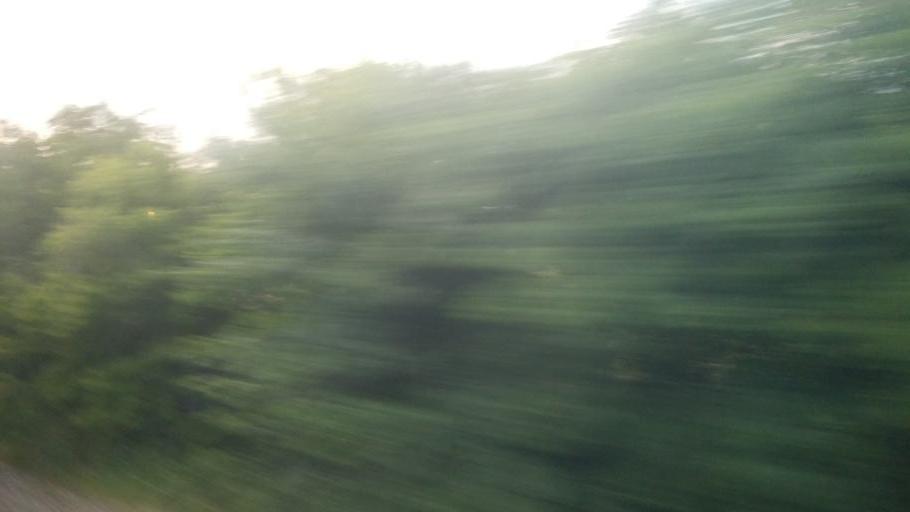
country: US
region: Kansas
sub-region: Marion County
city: Peabody
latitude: 38.1653
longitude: -97.0921
